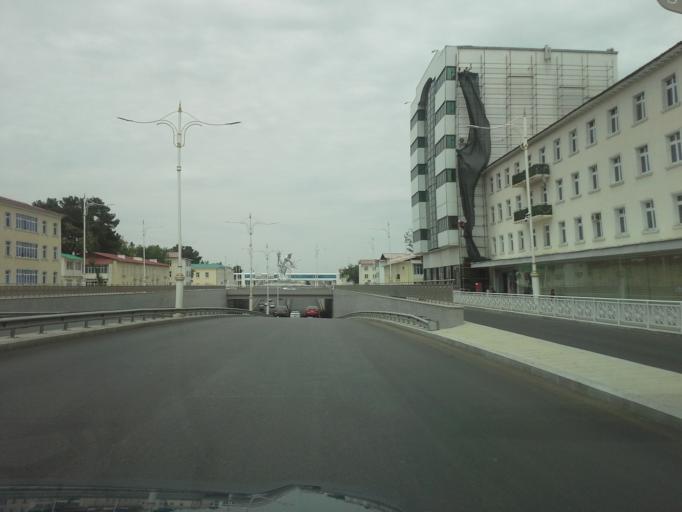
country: TM
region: Ahal
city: Ashgabat
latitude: 37.9351
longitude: 58.3965
